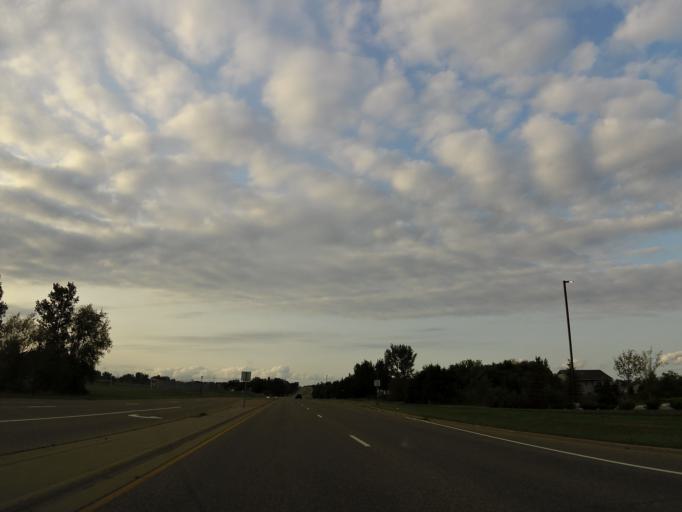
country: US
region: Minnesota
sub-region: Dakota County
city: Lakeville
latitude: 44.6617
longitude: -93.2527
